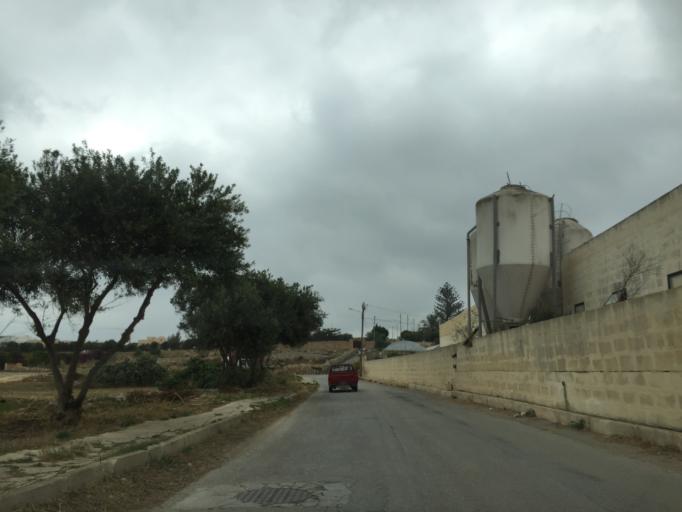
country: MT
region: L-Imgarr
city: Imgarr
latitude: 35.9161
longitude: 14.3724
